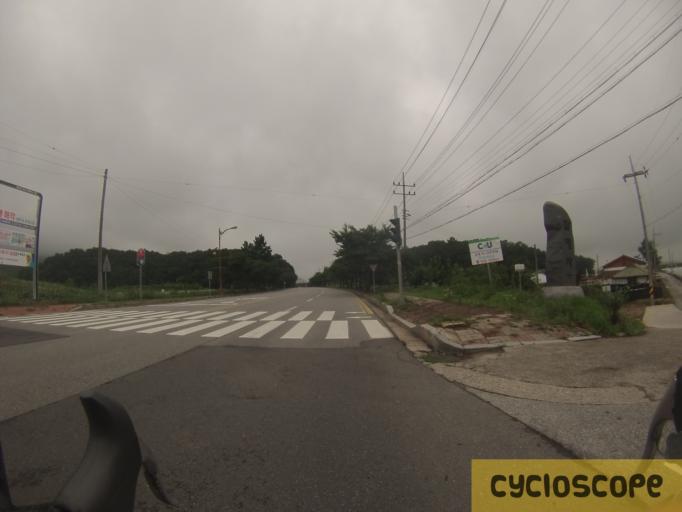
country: KR
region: Chungcheongnam-do
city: Asan
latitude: 36.8045
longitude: 126.9173
